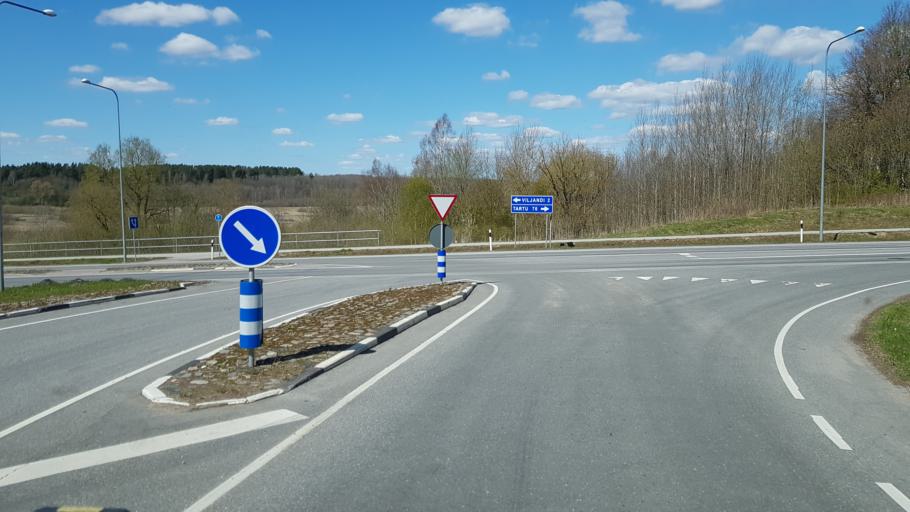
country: EE
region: Viljandimaa
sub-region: Viiratsi vald
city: Viiratsi
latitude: 58.3629
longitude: 25.6392
